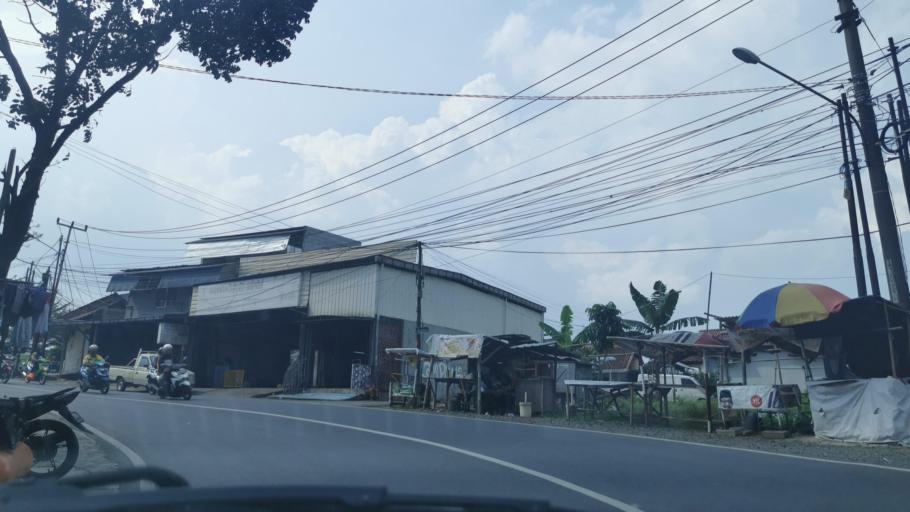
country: ID
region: West Java
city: Depok
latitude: -6.4080
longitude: 106.8348
